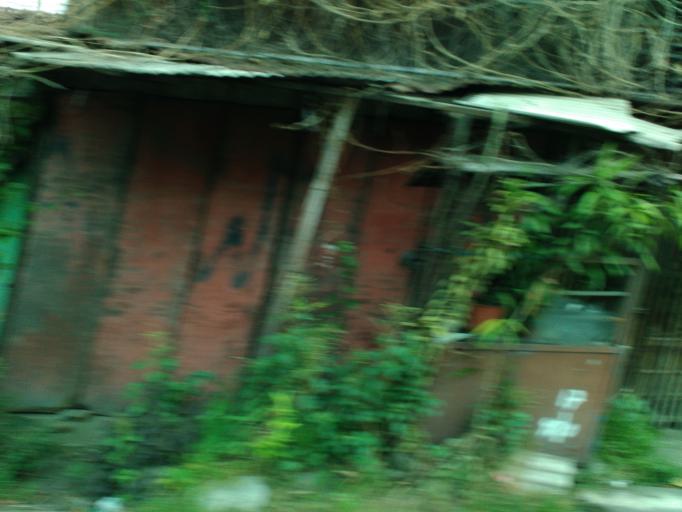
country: ID
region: Central Java
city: Gatak
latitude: -7.5945
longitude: 110.7028
